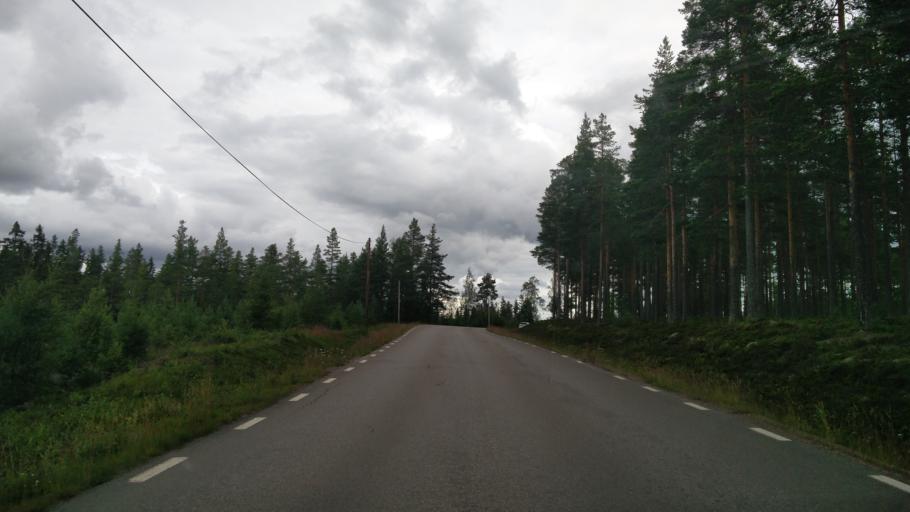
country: NO
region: Hedmark
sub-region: Trysil
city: Innbygda
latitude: 61.1618
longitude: 12.8222
